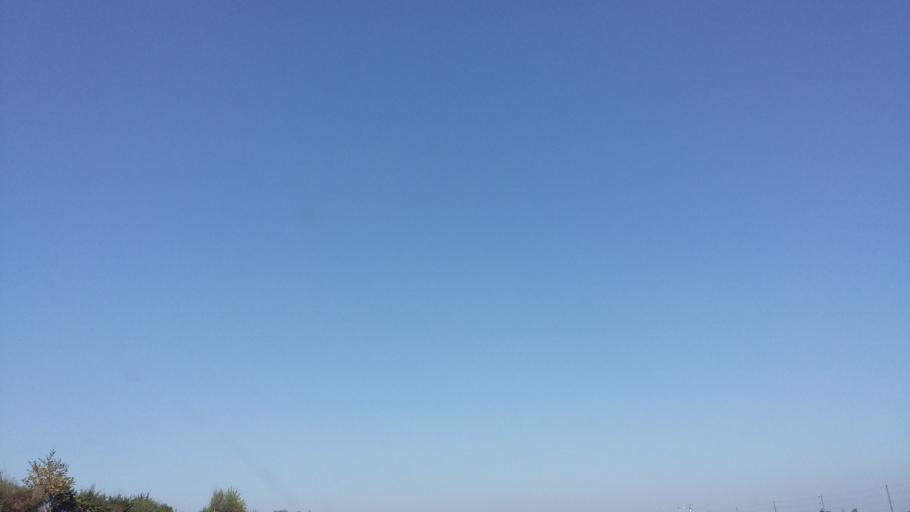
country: DE
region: Bavaria
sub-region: Upper Bavaria
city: Hurlach
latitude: 48.1147
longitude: 10.8352
